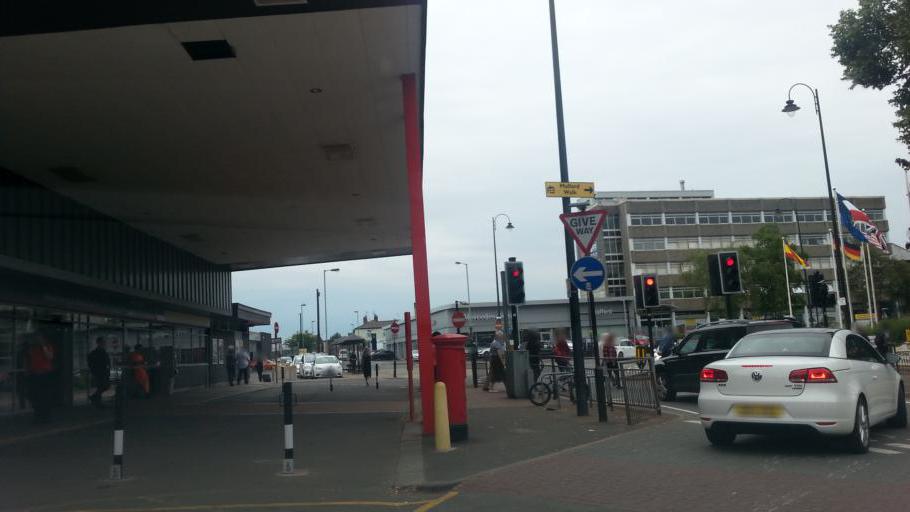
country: GB
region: England
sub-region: Staffordshire
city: Stafford
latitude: 52.8038
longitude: -2.1218
